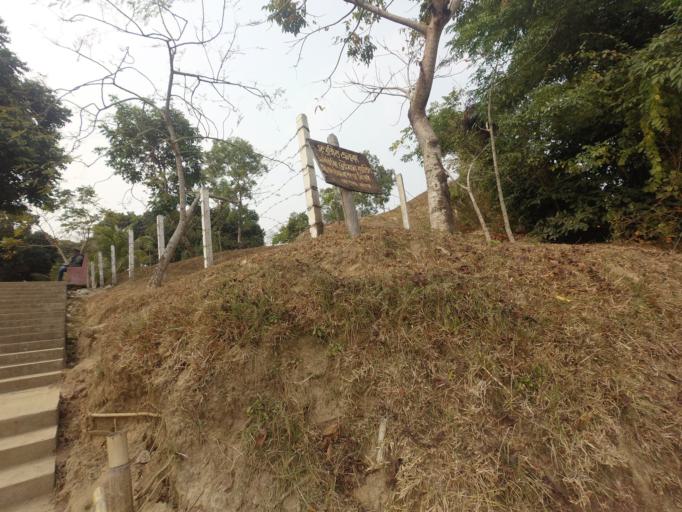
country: BD
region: Dhaka
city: Netrakona
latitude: 25.1776
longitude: 90.6570
